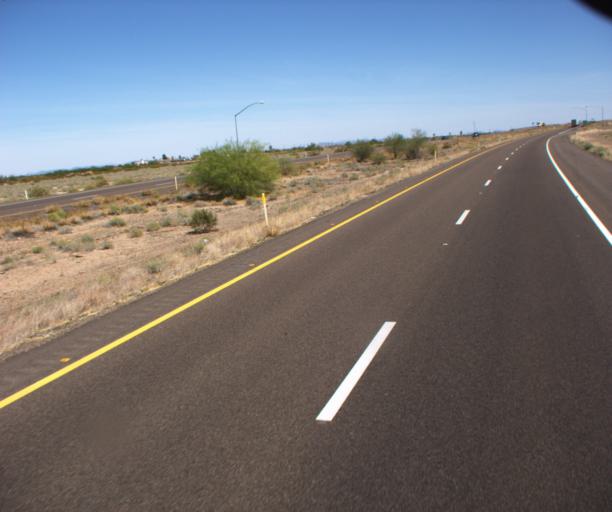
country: US
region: Arizona
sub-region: Yuma County
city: Wellton
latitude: 32.7977
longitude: -113.5472
